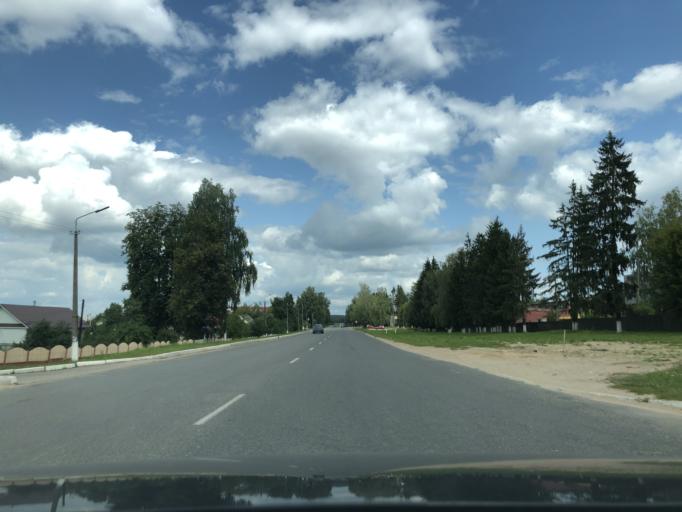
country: BY
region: Minsk
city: Lahoysk
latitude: 54.2128
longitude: 27.8517
